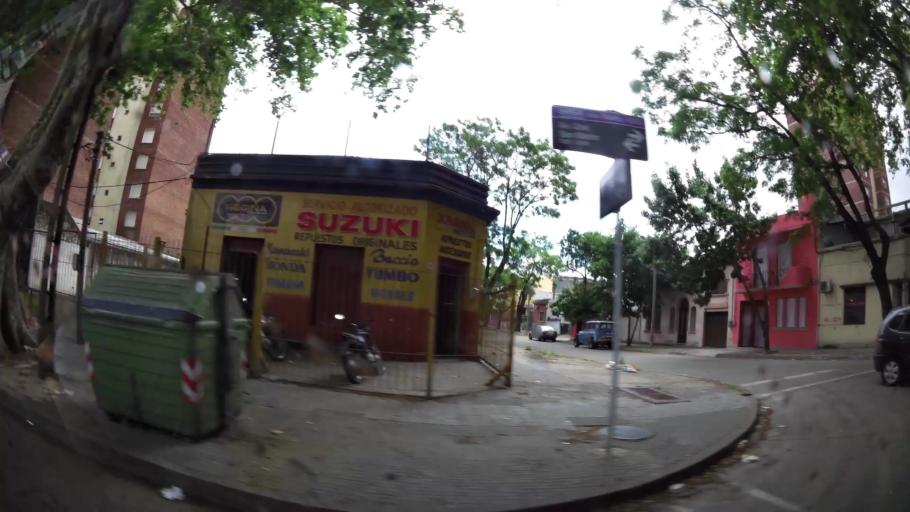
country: UY
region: Montevideo
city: Montevideo
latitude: -34.8598
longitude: -56.1774
